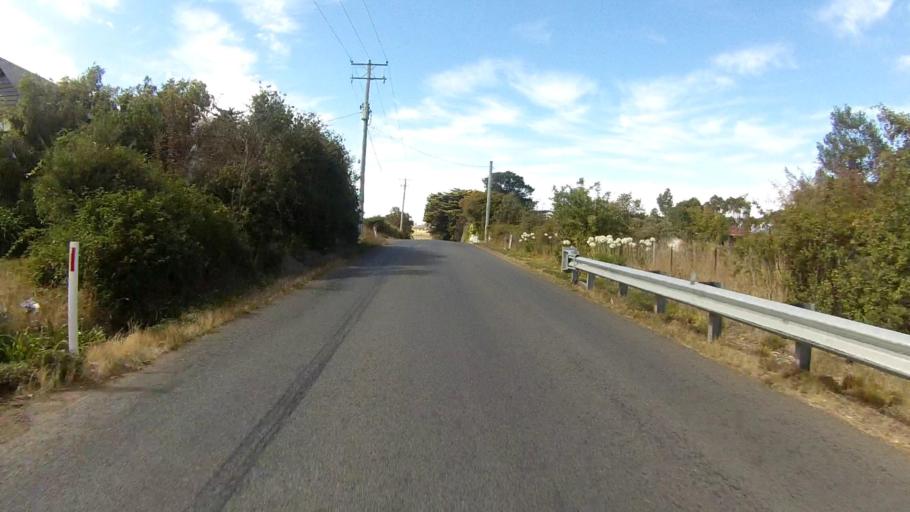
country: AU
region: Tasmania
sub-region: Brighton
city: Old Beach
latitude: -42.7540
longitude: 147.2792
